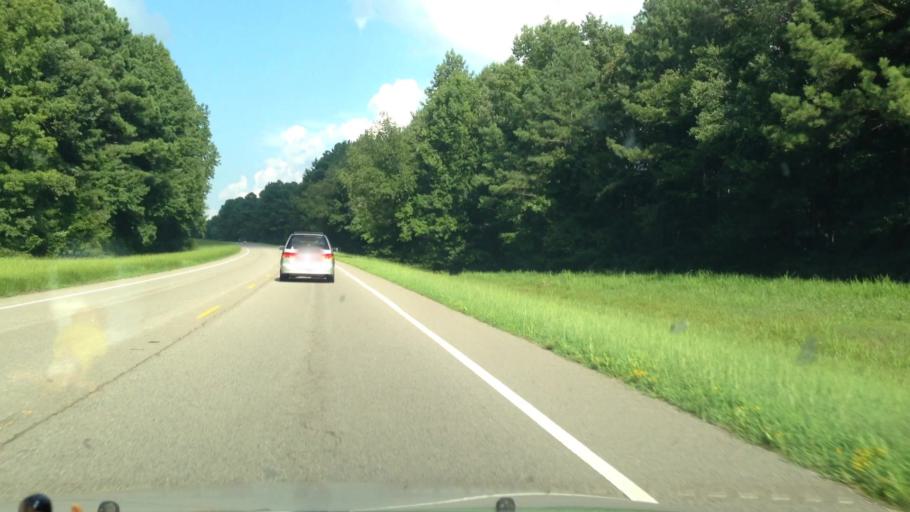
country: US
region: North Carolina
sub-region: Lee County
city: Broadway
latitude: 35.4378
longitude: -79.0623
